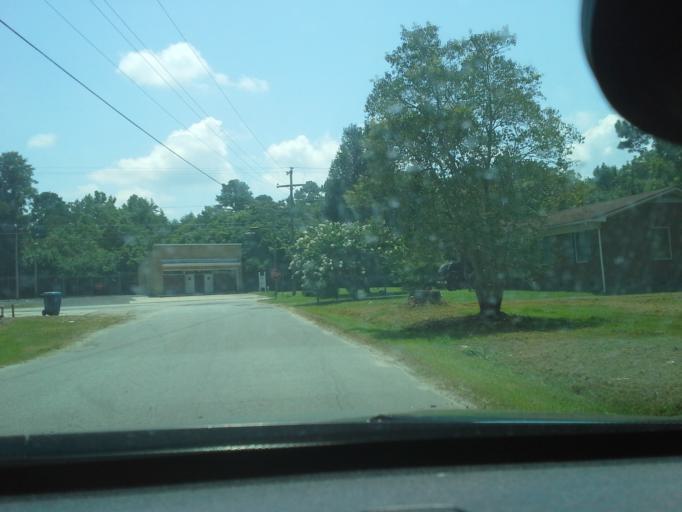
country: US
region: North Carolina
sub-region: Washington County
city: Plymouth
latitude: 35.8549
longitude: -76.7564
